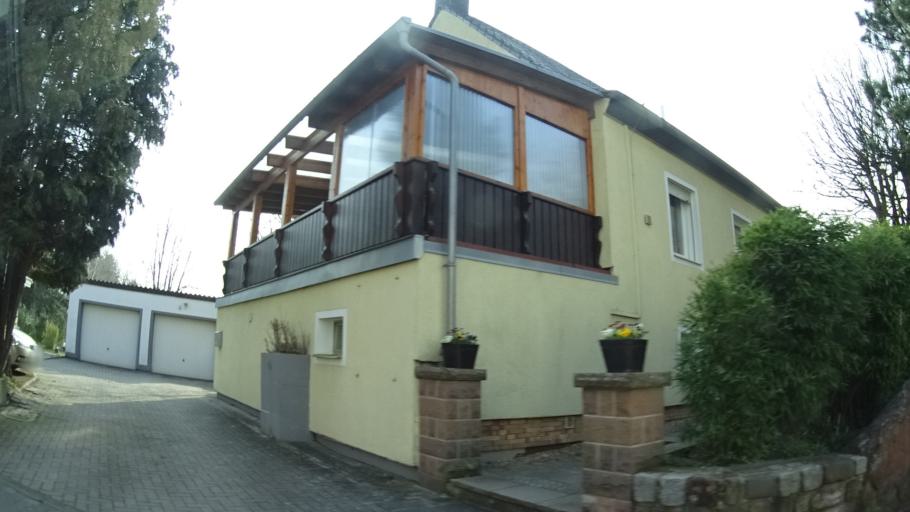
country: DE
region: Rheinland-Pfalz
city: Altenglan
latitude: 49.5544
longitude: 7.4667
